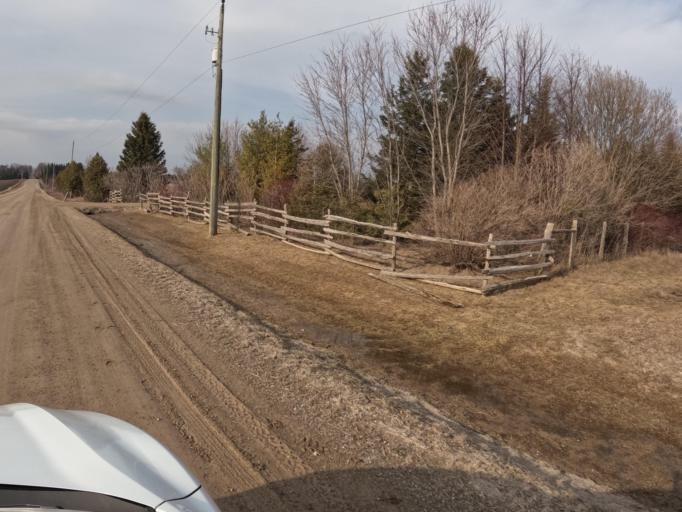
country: CA
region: Ontario
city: Orangeville
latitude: 43.9053
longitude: -80.2690
